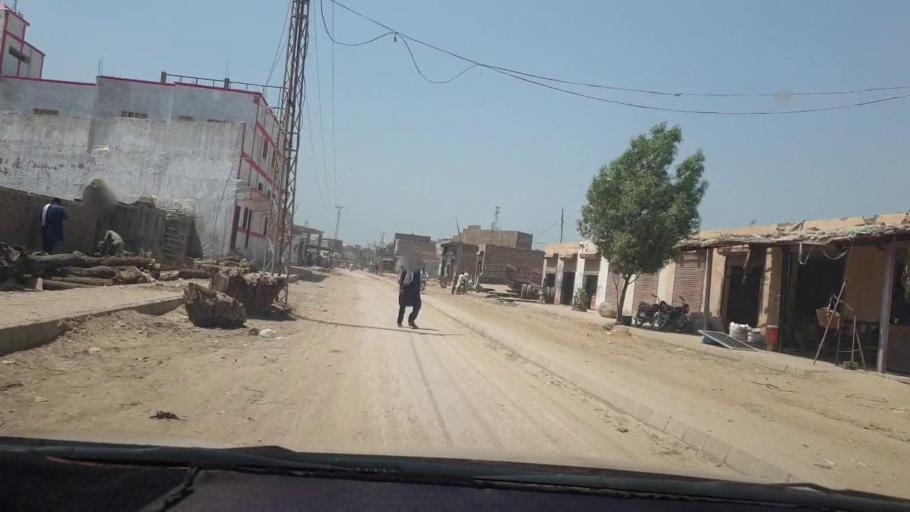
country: PK
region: Sindh
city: Kambar
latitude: 27.5907
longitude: 68.0082
